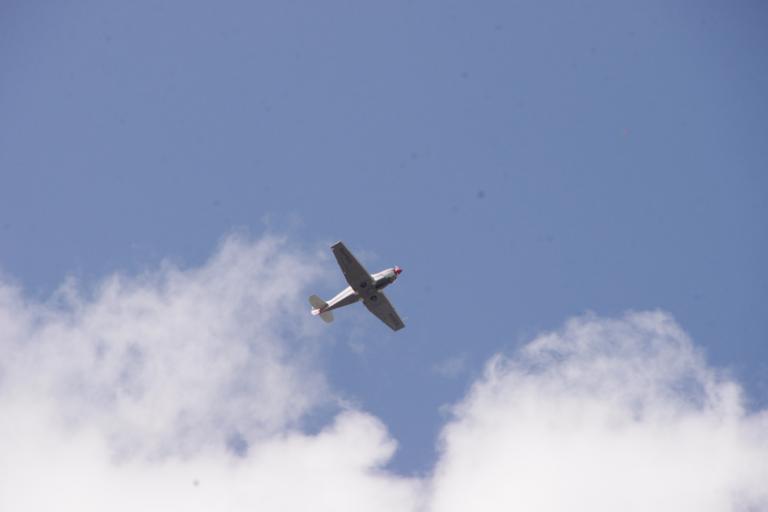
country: RU
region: Samara
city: Tol'yatti
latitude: 53.5516
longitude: 49.2557
